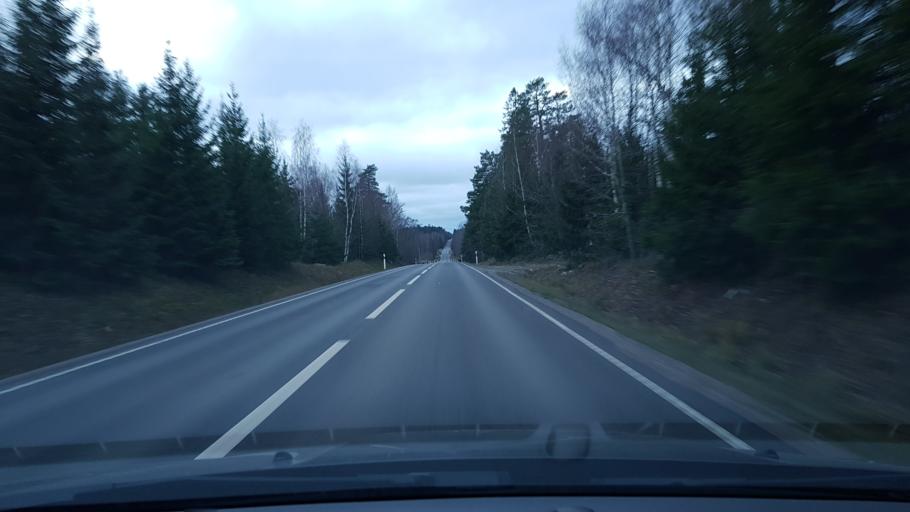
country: SE
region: Uppsala
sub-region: Uppsala Kommun
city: Vattholma
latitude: 59.9463
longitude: 17.9931
